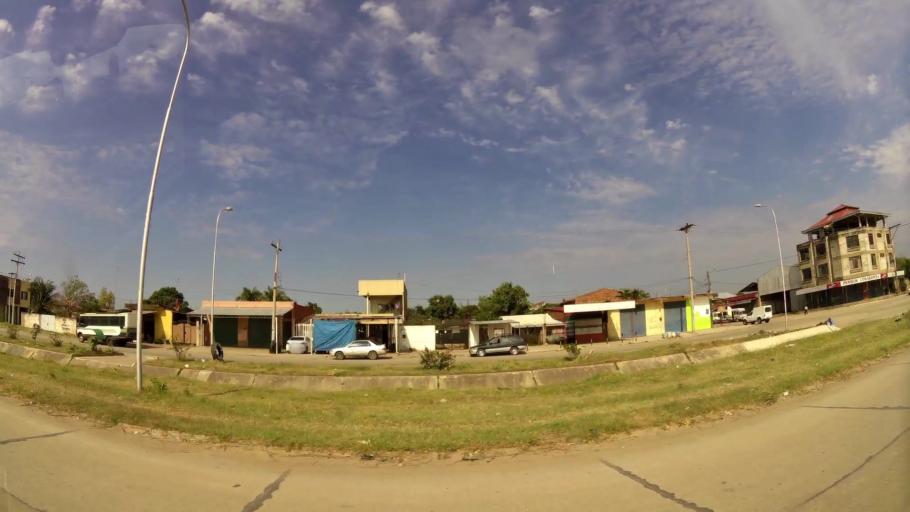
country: BO
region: Santa Cruz
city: Santa Cruz de la Sierra
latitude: -17.7269
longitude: -63.1381
